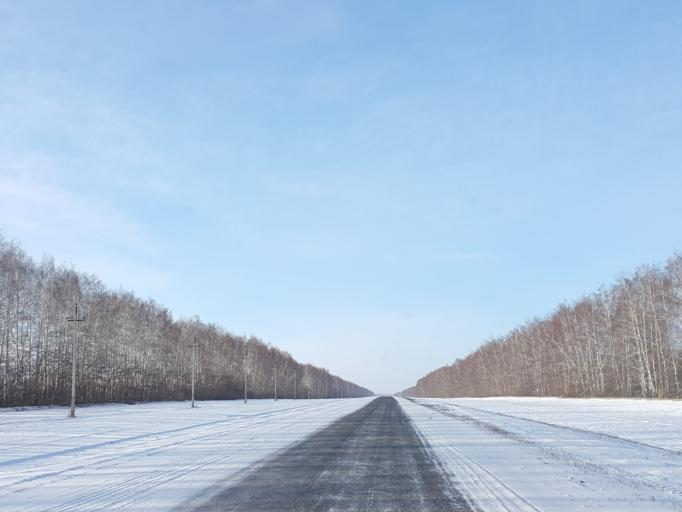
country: RU
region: Tambov
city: Znamenka
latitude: 52.3719
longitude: 41.2936
